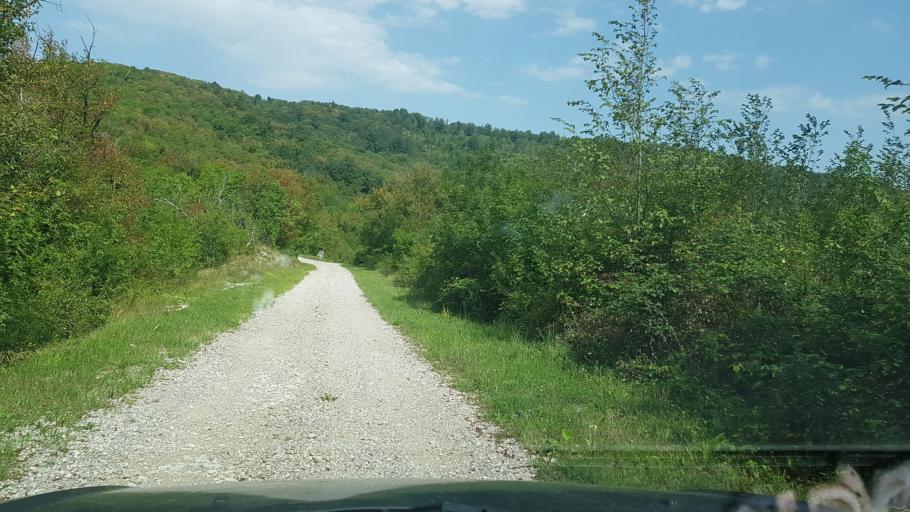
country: SI
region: Nova Gorica
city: Solkan
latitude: 46.0079
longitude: 13.6437
